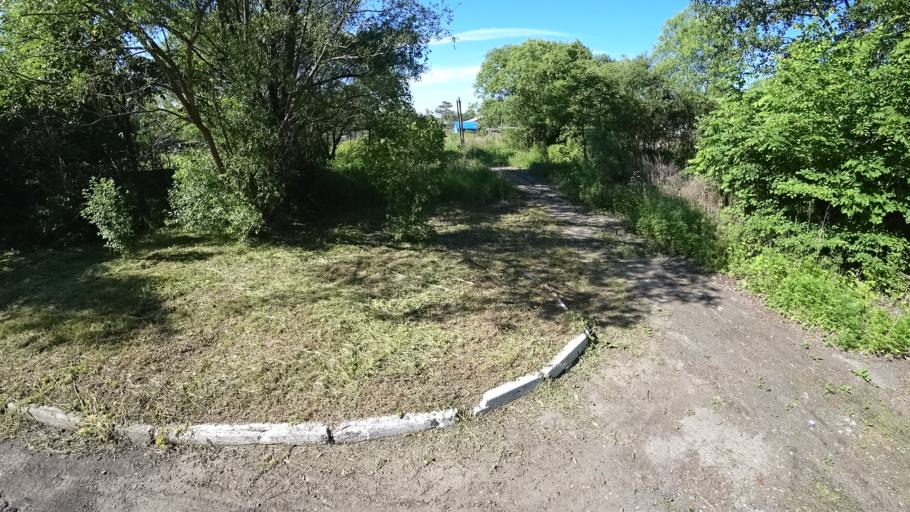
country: RU
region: Khabarovsk Krai
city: Khor
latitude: 47.8865
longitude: 134.9971
